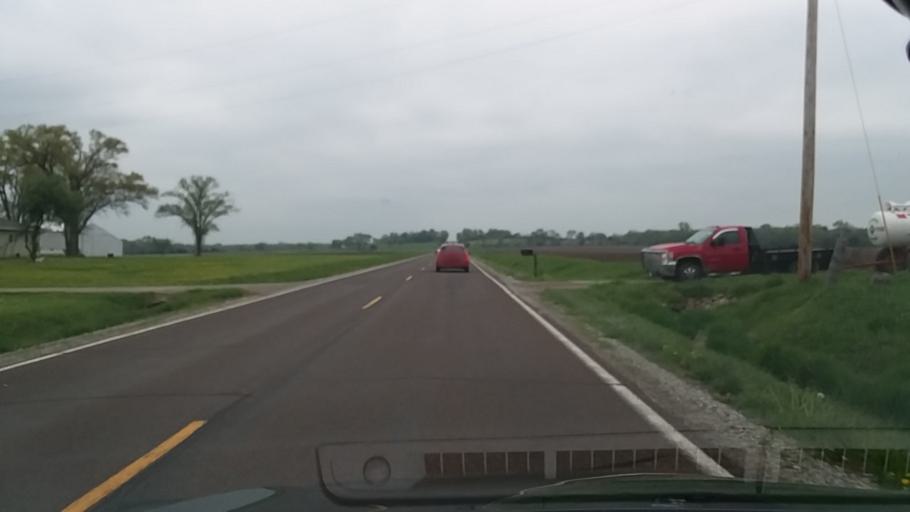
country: US
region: Kansas
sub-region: Douglas County
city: Eudora
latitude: 38.8517
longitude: -95.0932
